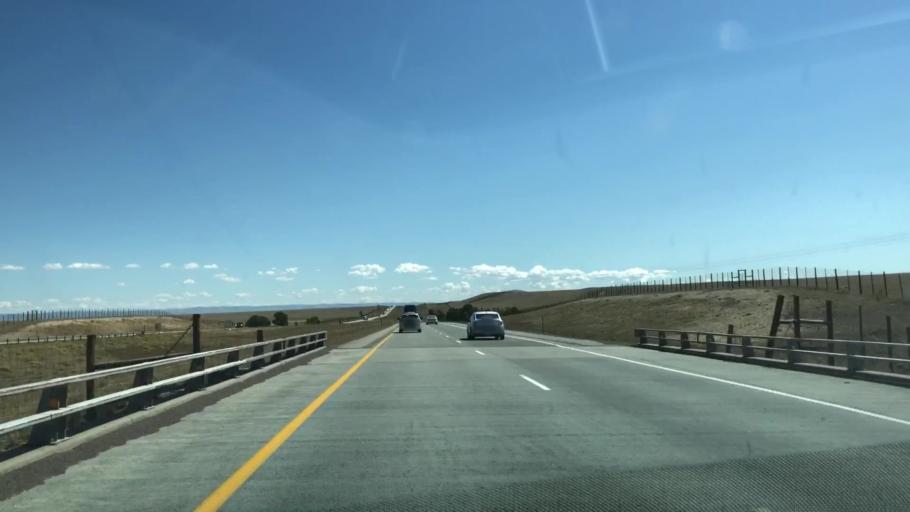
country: US
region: Wyoming
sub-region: Albany County
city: Laramie
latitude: 41.4845
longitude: -106.0253
